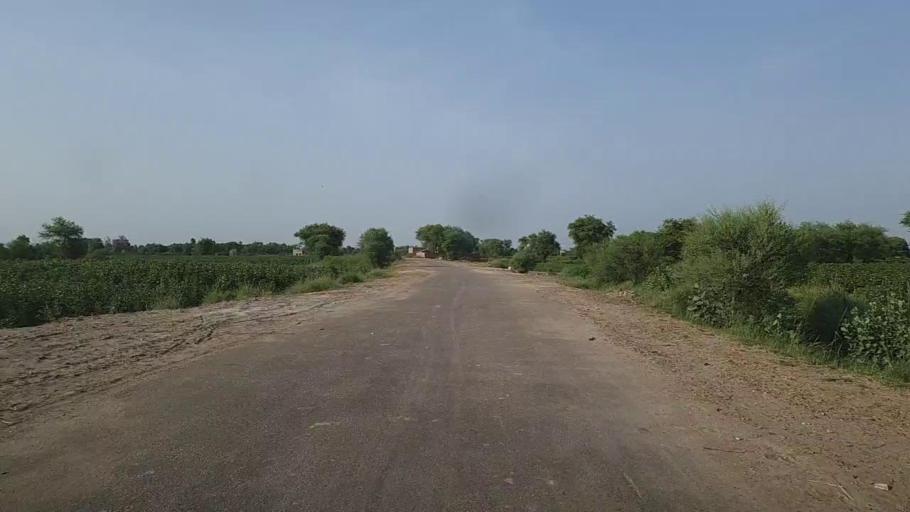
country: PK
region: Sindh
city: Ubauro
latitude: 28.0948
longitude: 69.8453
